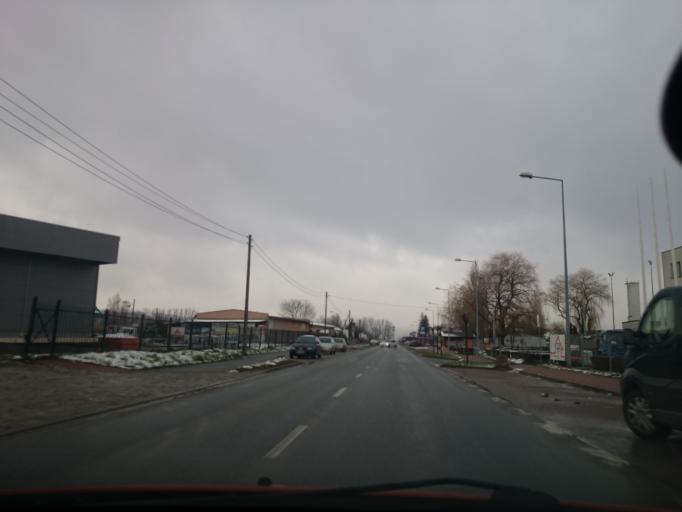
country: PL
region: Lower Silesian Voivodeship
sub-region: Powiat klodzki
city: Klodzko
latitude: 50.4436
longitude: 16.6360
